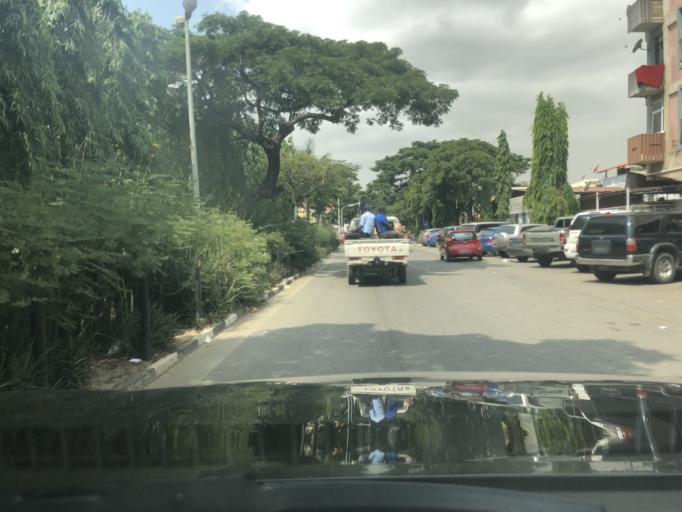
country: AO
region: Luanda
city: Luanda
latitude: -8.8264
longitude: 13.2480
